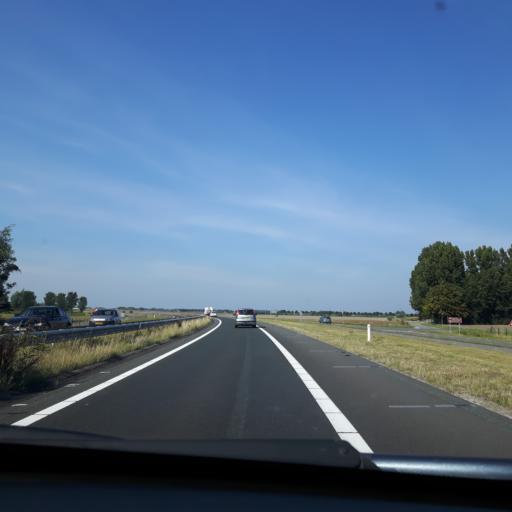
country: BE
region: Flanders
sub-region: Provincie Oost-Vlaanderen
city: Sint-Laureins
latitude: 51.3277
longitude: 3.5927
